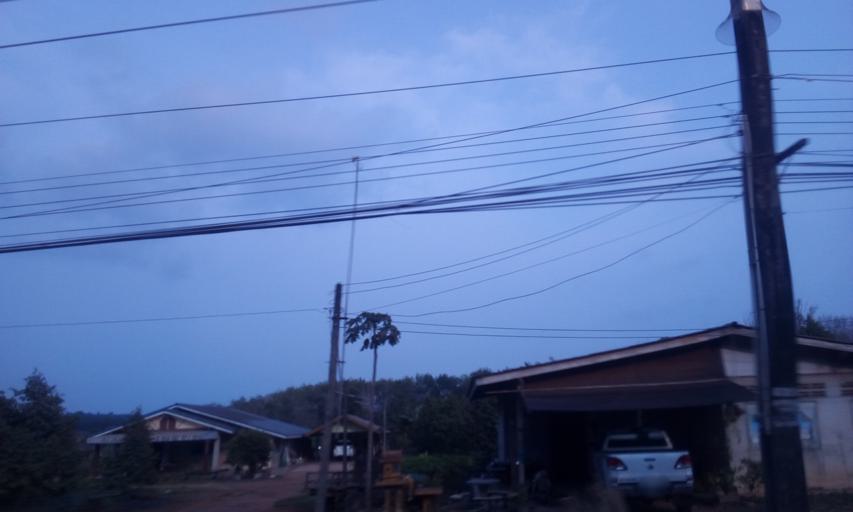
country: TH
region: Trat
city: Khao Saming
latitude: 12.3564
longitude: 102.3821
